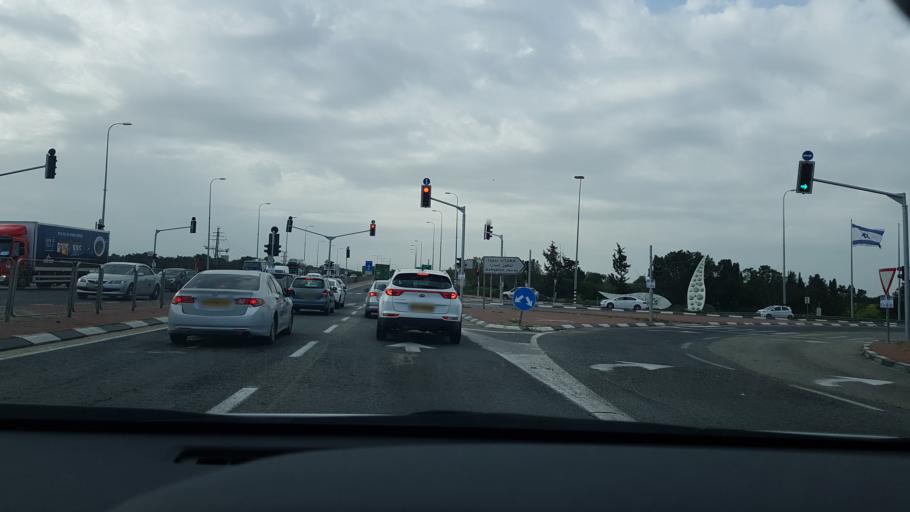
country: IL
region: Southern District
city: Ashqelon
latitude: 31.6810
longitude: 34.6097
